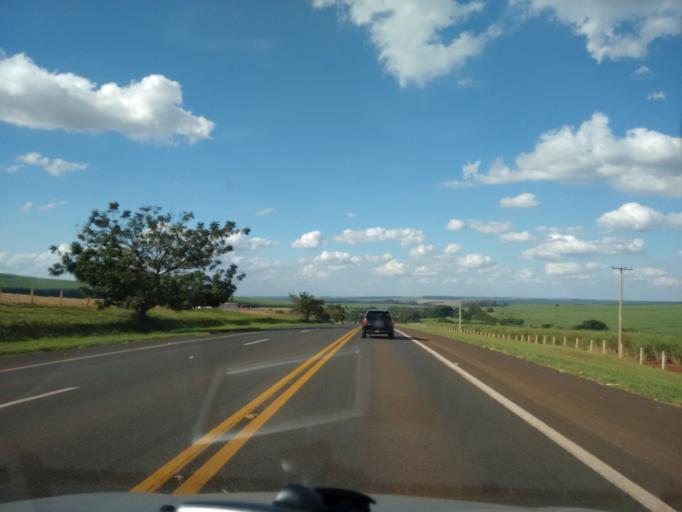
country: BR
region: Sao Paulo
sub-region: Americo Brasiliense
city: Americo Brasiliense
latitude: -21.7634
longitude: -48.0809
